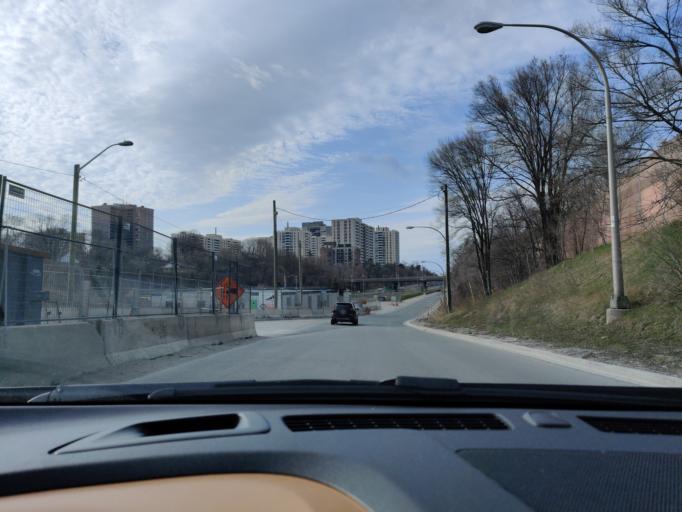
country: CA
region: Ontario
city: Toronto
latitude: 43.6997
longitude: -79.4355
